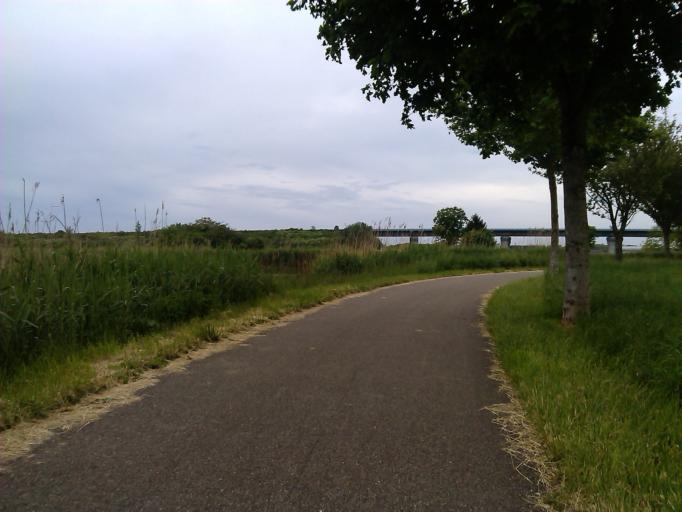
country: FR
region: Franche-Comte
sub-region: Departement du Jura
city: Choisey
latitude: 47.0555
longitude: 5.4444
